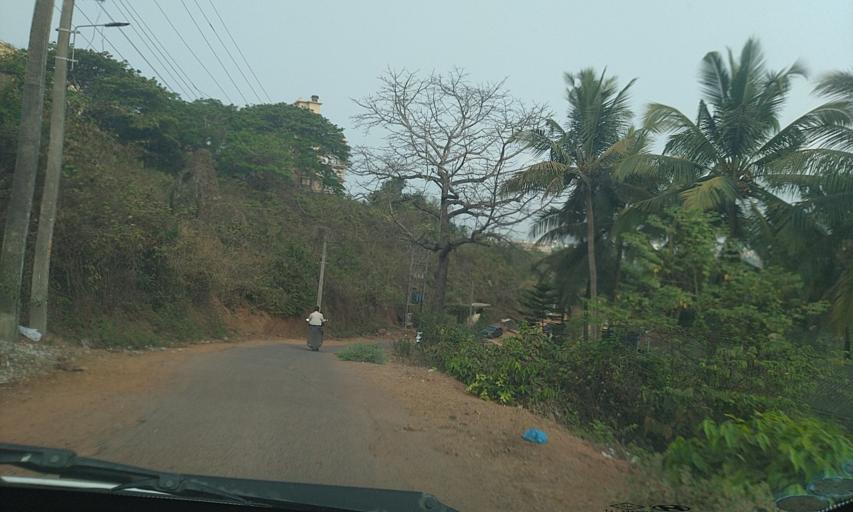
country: IN
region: Goa
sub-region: North Goa
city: Taleigao
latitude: 15.4632
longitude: 73.8164
